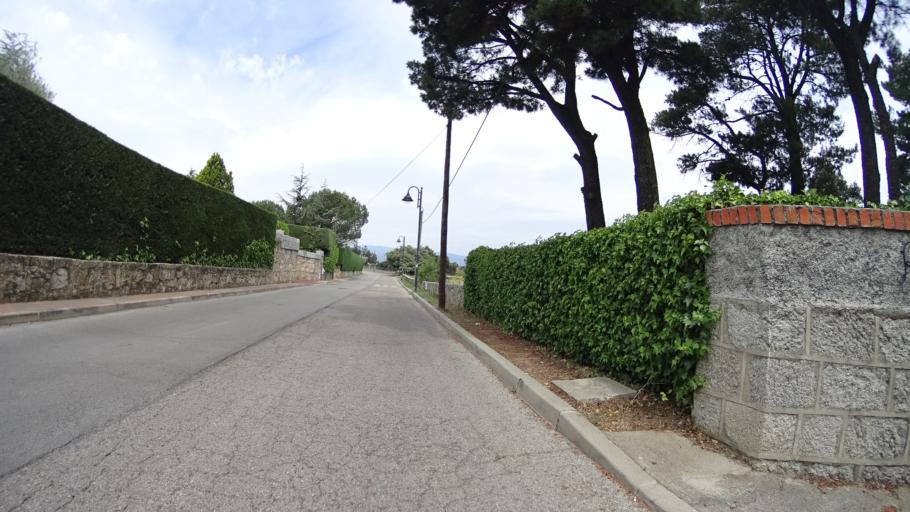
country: ES
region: Madrid
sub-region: Provincia de Madrid
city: Galapagar
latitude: 40.5692
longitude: -4.0055
